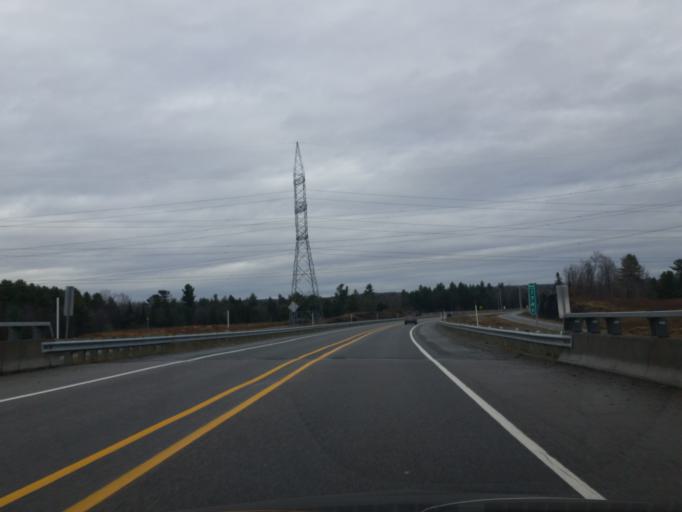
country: CA
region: Ontario
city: Clarence-Rockland
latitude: 45.6074
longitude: -75.3879
